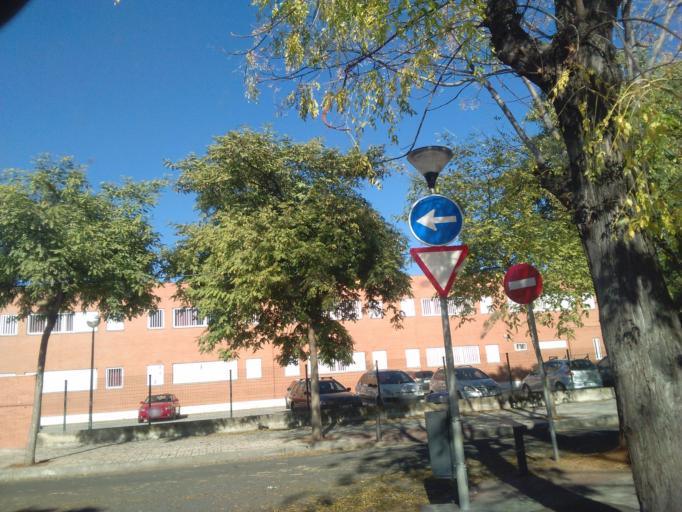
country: ES
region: Andalusia
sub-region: Provincia de Sevilla
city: Sevilla
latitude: 37.3918
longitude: -5.9151
